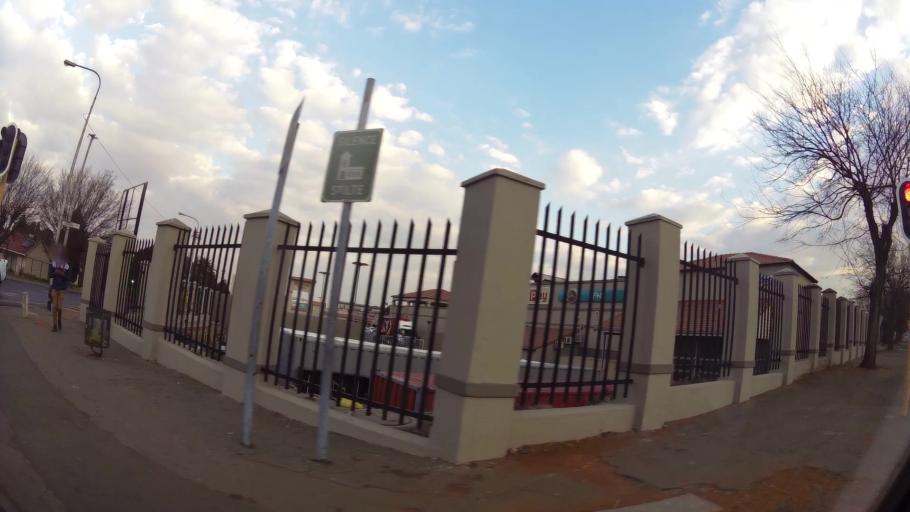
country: ZA
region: Gauteng
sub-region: Ekurhuleni Metropolitan Municipality
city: Germiston
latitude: -26.1848
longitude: 28.1585
